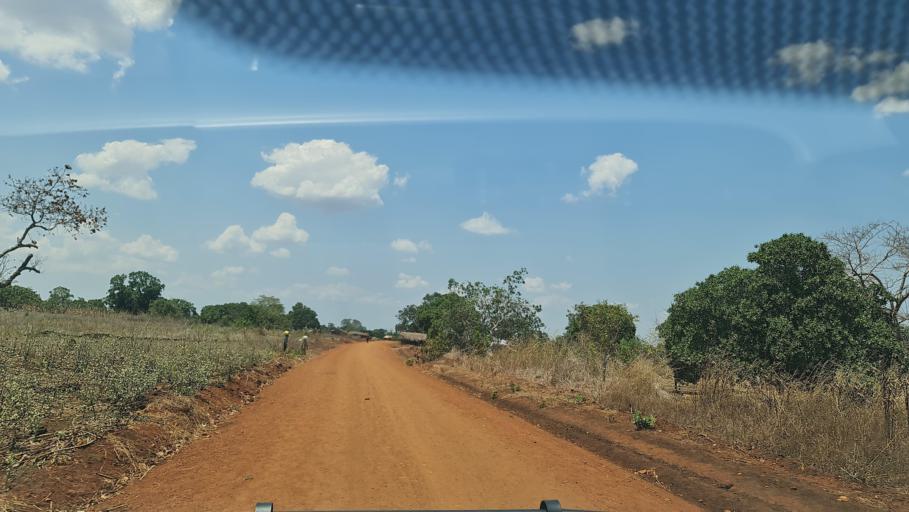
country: MZ
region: Nampula
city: Nacala
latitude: -14.8058
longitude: 40.0711
